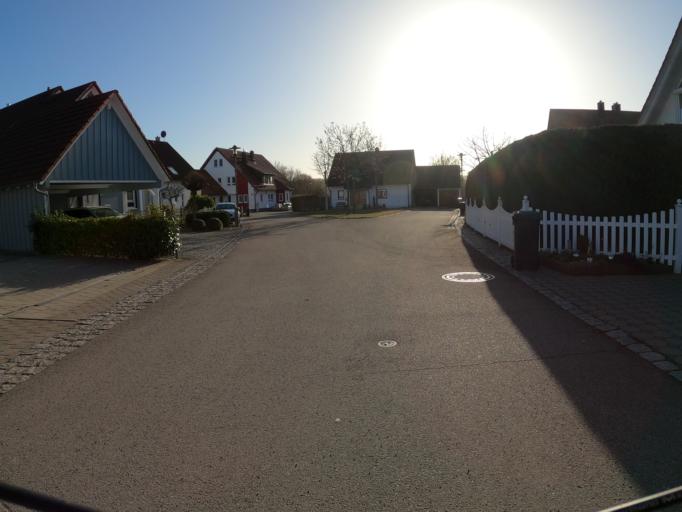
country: DE
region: Bavaria
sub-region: Swabia
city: Holzheim
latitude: 48.4008
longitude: 10.1019
